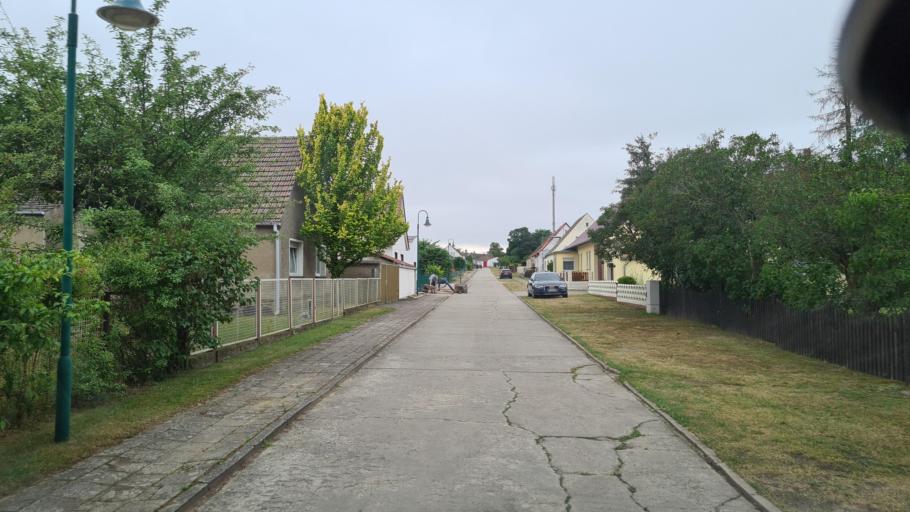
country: DE
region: Brandenburg
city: Ihlow
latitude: 51.9653
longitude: 13.2564
